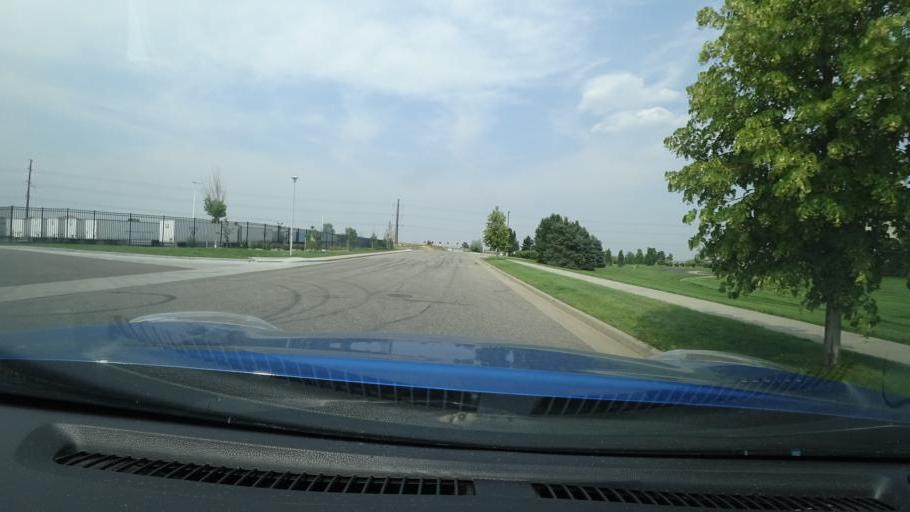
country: US
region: Colorado
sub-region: Adams County
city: Aurora
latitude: 39.7675
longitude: -104.7403
